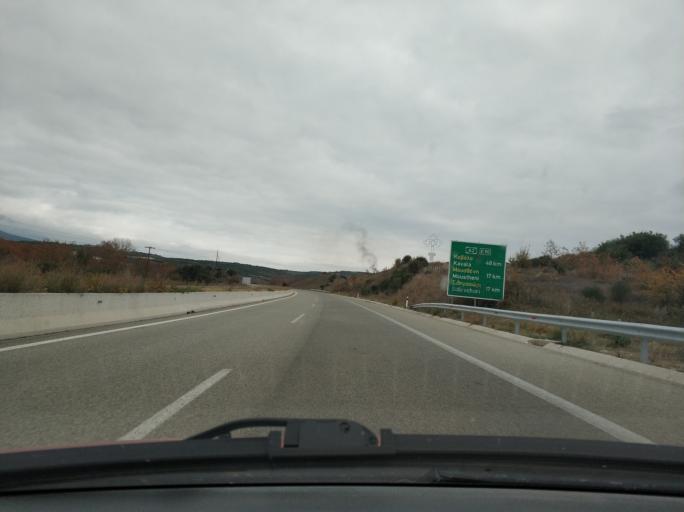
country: GR
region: East Macedonia and Thrace
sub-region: Nomos Kavalas
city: Paralia Ofryniou
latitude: 40.7891
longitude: 23.9696
